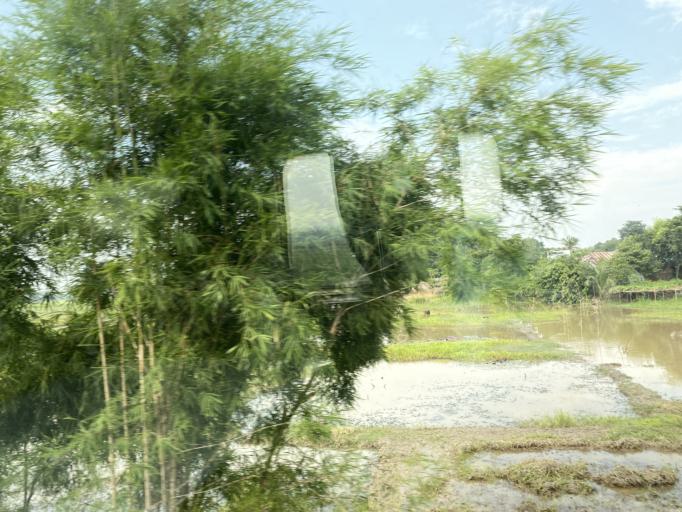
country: IN
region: Tripura
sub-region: West Tripura
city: Agartala
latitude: 23.9945
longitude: 91.2872
